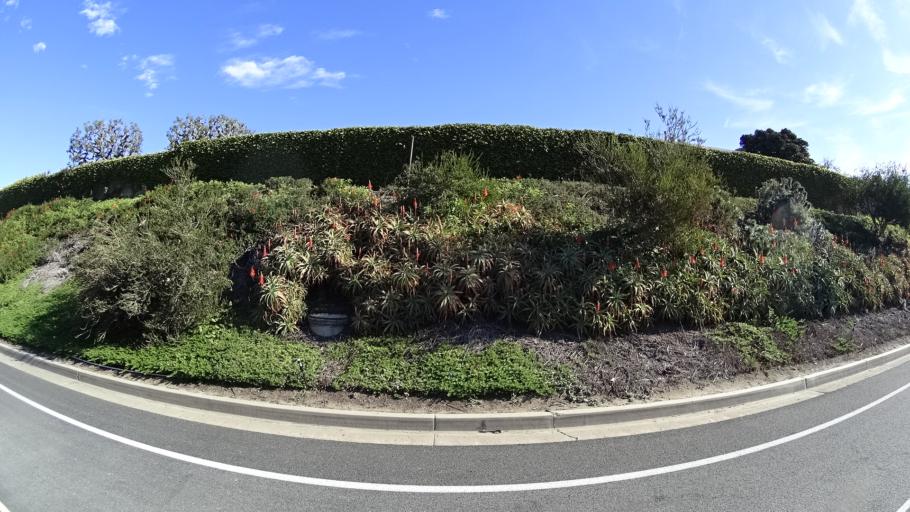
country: US
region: California
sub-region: Orange County
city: Dana Point
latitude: 33.4728
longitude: -117.7146
